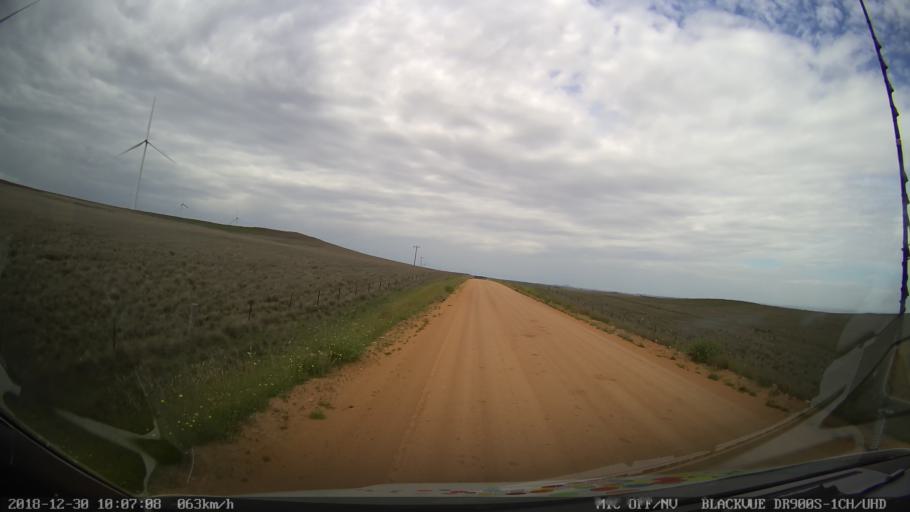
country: AU
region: New South Wales
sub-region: Cooma-Monaro
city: Cooma
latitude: -36.5374
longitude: 149.1249
